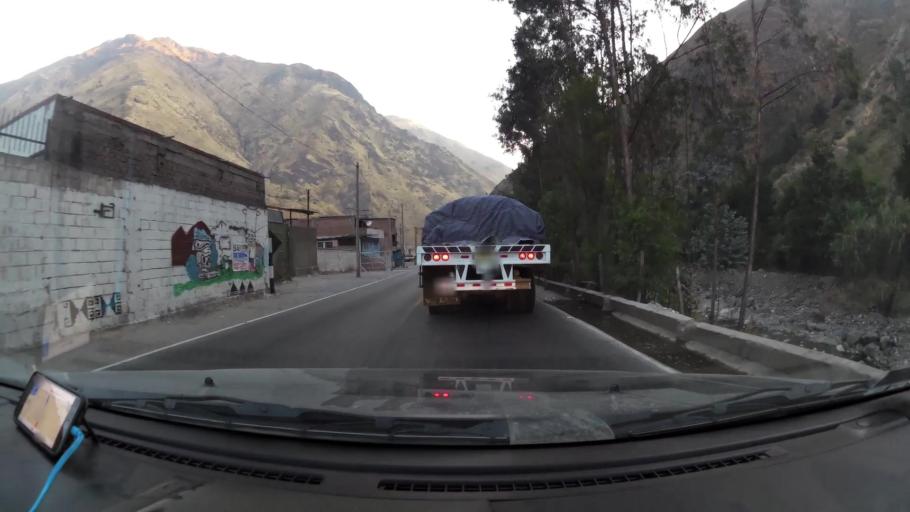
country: PE
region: Lima
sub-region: Provincia de Huarochiri
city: Matucana
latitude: -11.8453
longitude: -76.3879
